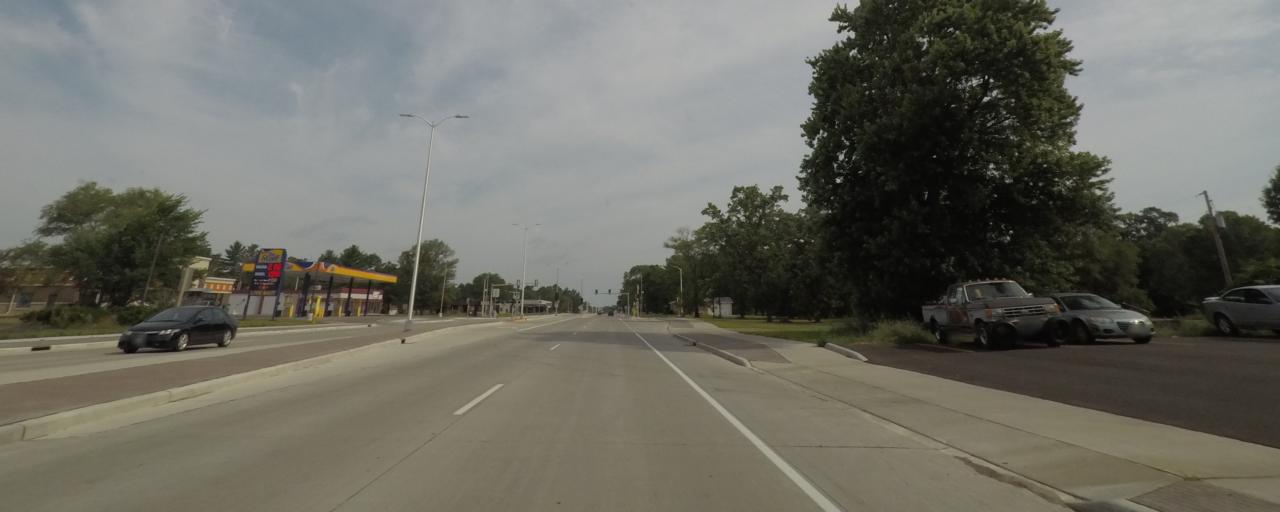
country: US
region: Wisconsin
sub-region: Portage County
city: Whiting
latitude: 44.4803
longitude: -89.5490
